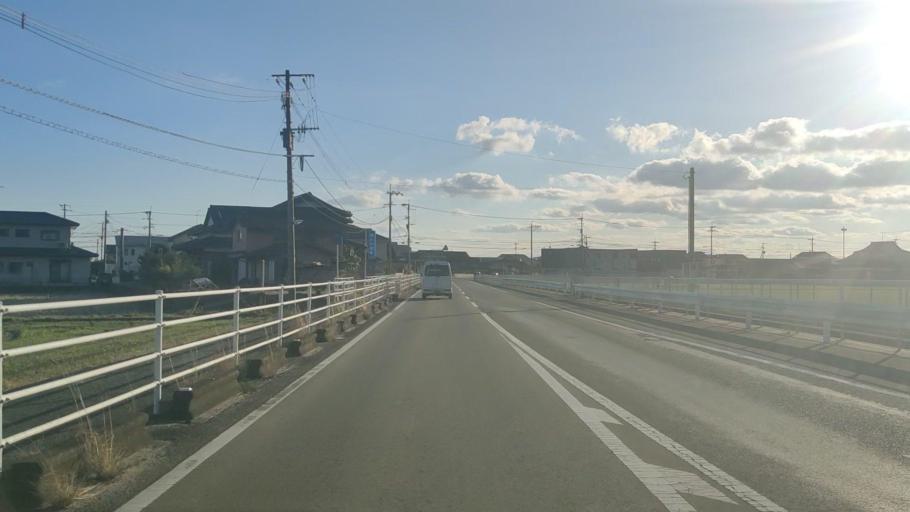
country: JP
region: Saga Prefecture
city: Saga-shi
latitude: 33.2779
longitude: 130.2231
